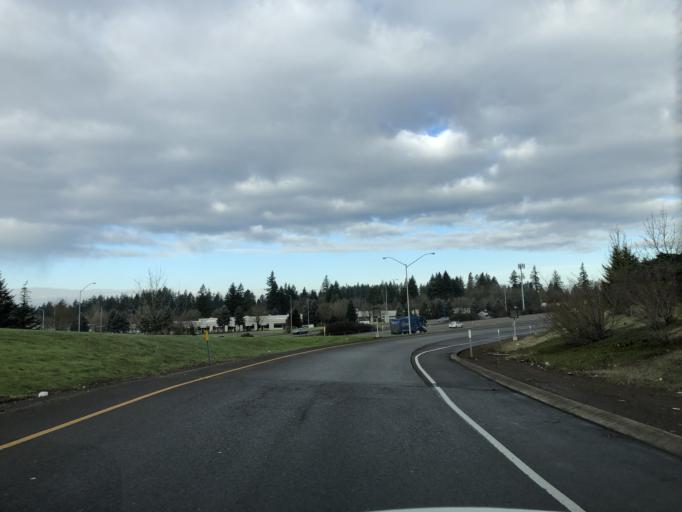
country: US
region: Oregon
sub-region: Clackamas County
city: Wilsonville
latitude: 45.3361
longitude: -122.7680
